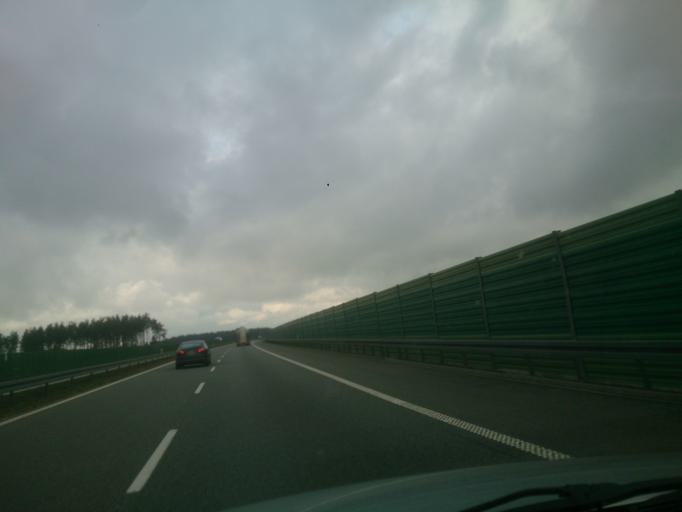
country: PL
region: Pomeranian Voivodeship
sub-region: Powiat tczewski
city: Pelplin
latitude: 53.9924
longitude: 18.6565
